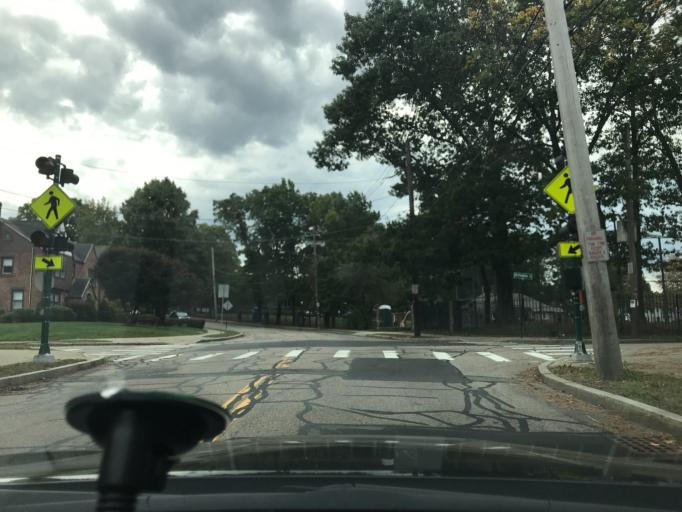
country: US
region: Massachusetts
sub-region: Middlesex County
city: Watertown
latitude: 42.3532
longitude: -71.1797
